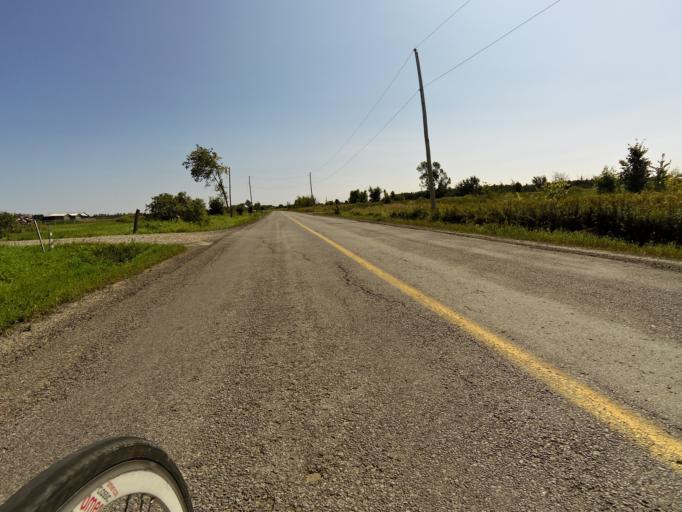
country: CA
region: Ontario
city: Arnprior
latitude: 45.4511
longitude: -76.0849
